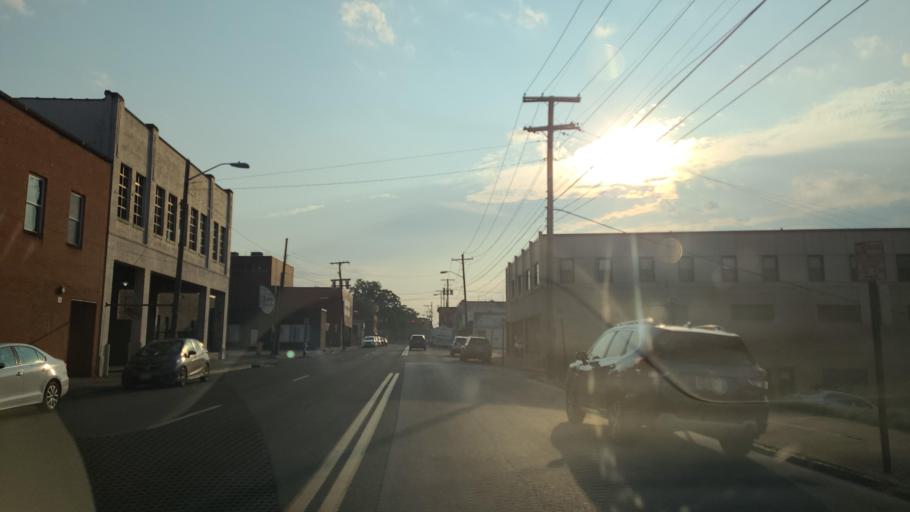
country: US
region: Virginia
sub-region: City of Roanoke
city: Roanoke
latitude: 37.2714
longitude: -79.9482
